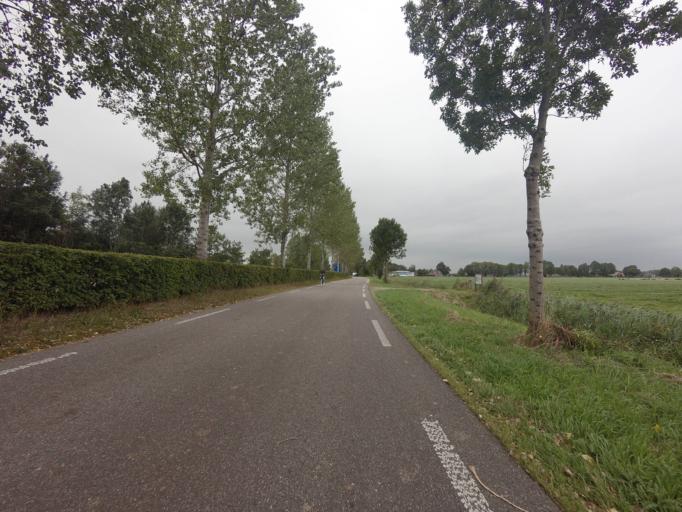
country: NL
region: Friesland
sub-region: Gemeente Opsterland
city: Tijnje
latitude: 53.0167
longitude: 6.0257
